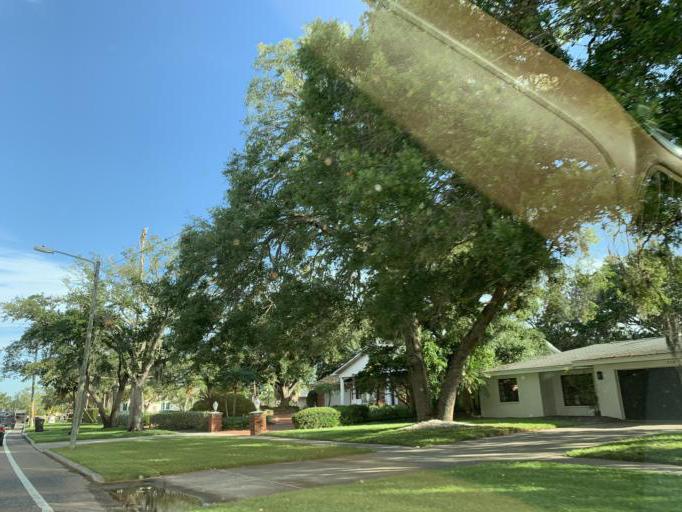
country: US
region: Florida
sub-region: Pinellas County
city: Saint Petersburg
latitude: 27.7959
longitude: -82.6197
